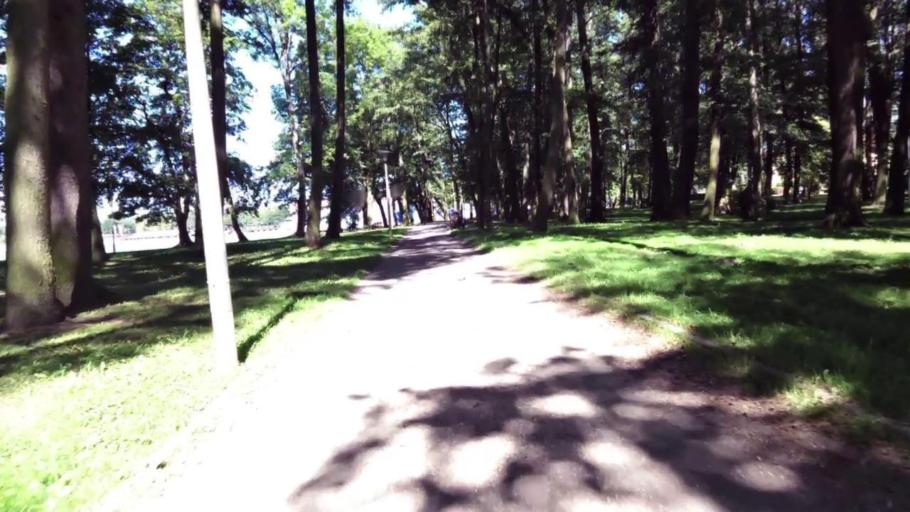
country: PL
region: West Pomeranian Voivodeship
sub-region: Powiat szczecinecki
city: Szczecinek
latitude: 53.7013
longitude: 16.6925
